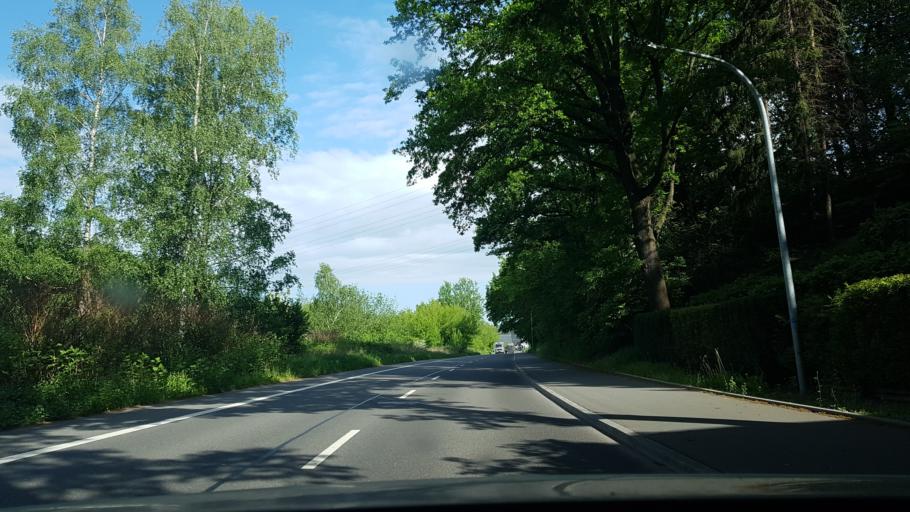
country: DE
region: Saxony
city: Wittgensdorf
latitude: 50.8794
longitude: 12.9019
